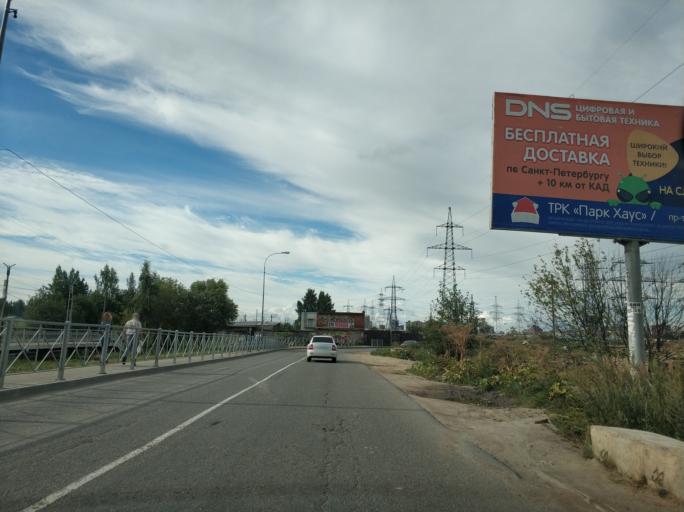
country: RU
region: Leningrad
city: Murino
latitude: 60.0499
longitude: 30.4412
